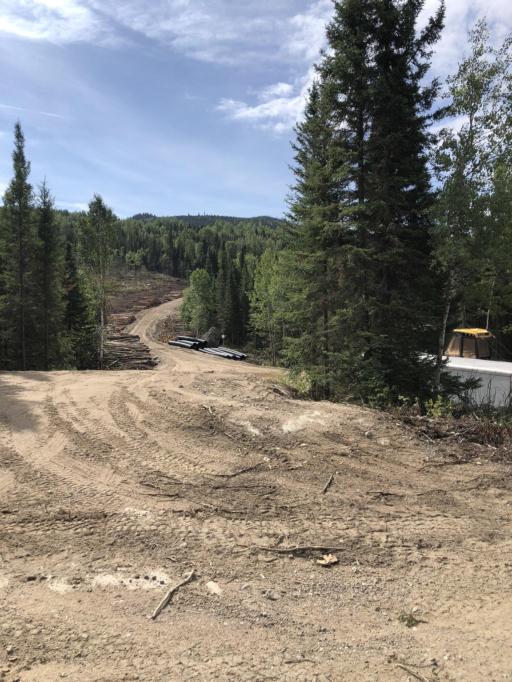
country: CA
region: Quebec
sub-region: Capitale-Nationale
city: La Malbaie
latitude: 48.0269
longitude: -70.5598
